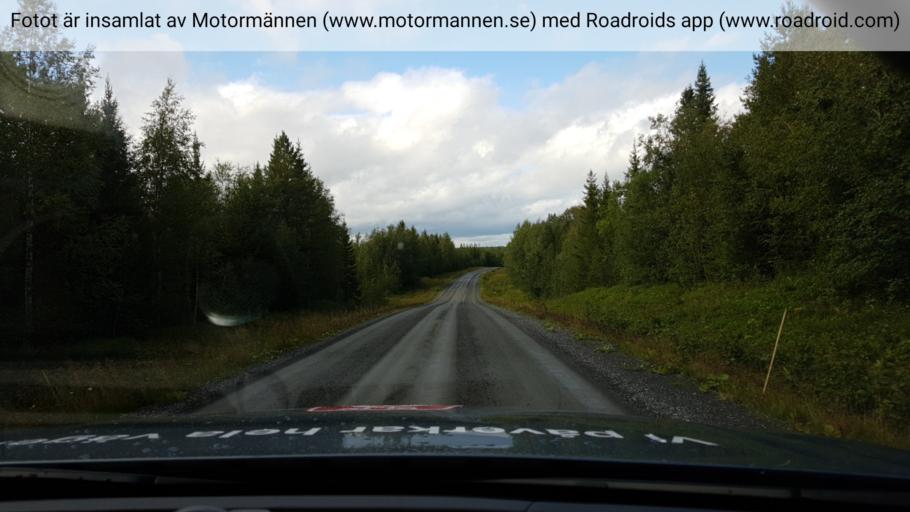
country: SE
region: Jaemtland
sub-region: Krokoms Kommun
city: Krokom
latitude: 63.7142
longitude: 14.5207
